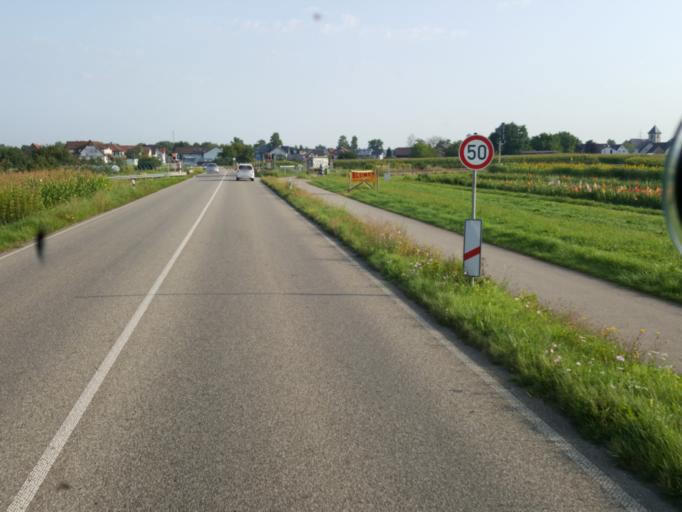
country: DE
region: Baden-Wuerttemberg
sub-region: Freiburg Region
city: Appenweier
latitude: 48.5532
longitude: 7.9795
